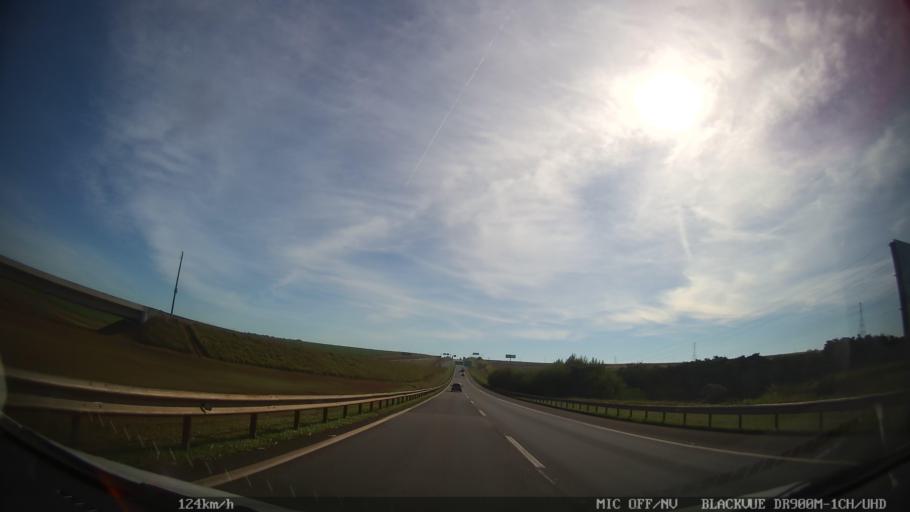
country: BR
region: Sao Paulo
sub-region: Cordeiropolis
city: Cordeiropolis
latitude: -22.4822
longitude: -47.3991
